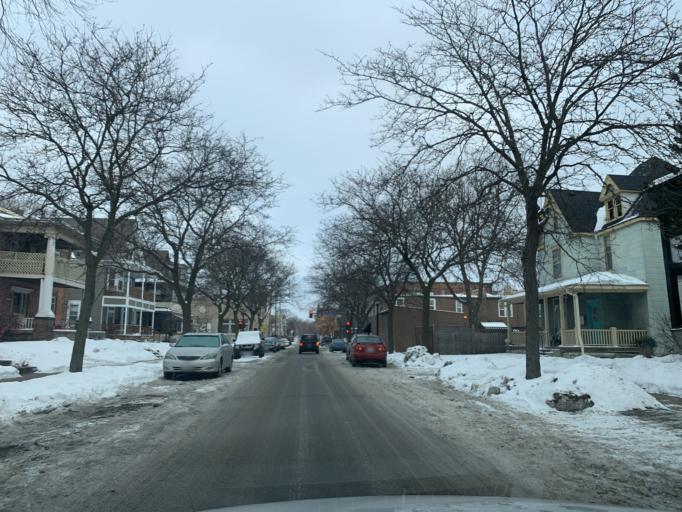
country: US
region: Minnesota
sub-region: Hennepin County
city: Minneapolis
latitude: 44.9583
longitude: -93.2931
